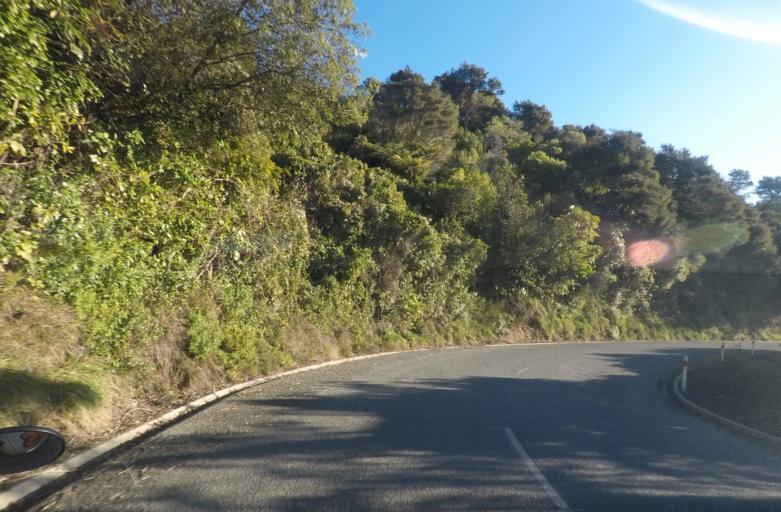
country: NZ
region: Marlborough
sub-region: Marlborough District
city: Picton
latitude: -41.2691
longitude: 173.9707
